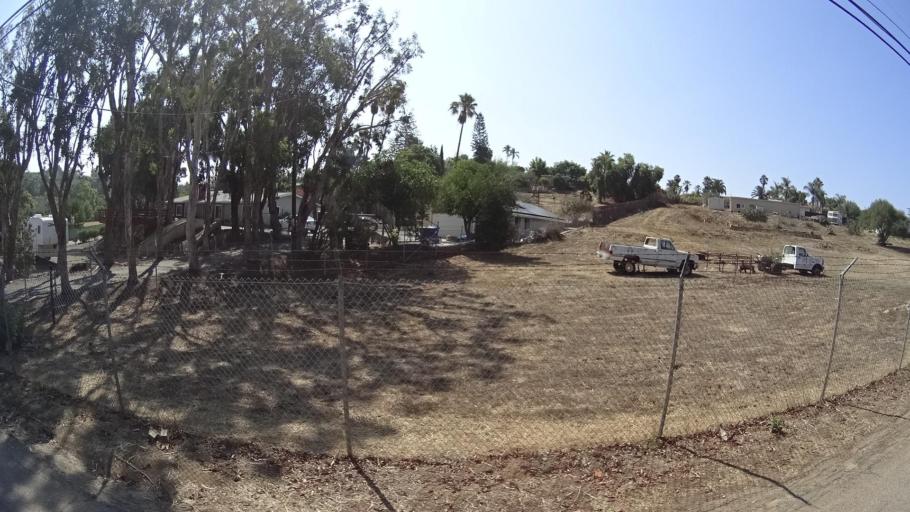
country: US
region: California
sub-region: San Diego County
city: Bonsall
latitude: 33.2497
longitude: -117.2318
